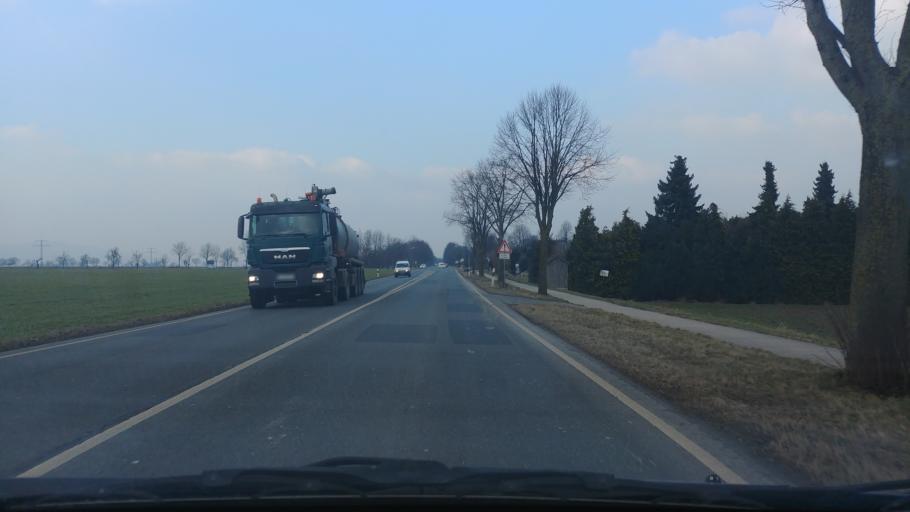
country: DE
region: Lower Saxony
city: Banteln
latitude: 52.0615
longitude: 9.7509
